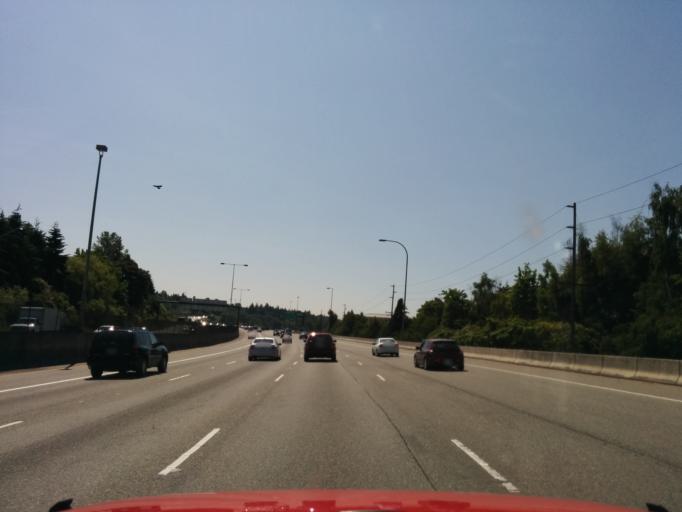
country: US
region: Washington
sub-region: King County
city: Bellevue
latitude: 47.6079
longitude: -122.1879
